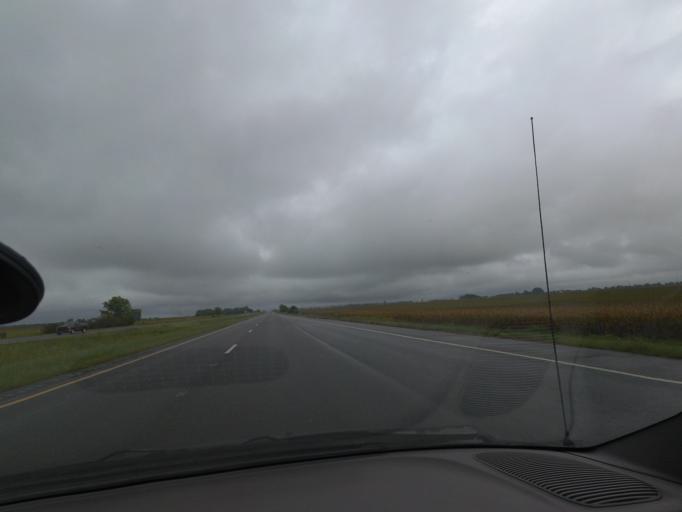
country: US
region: Illinois
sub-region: Champaign County
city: Mahomet
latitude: 40.1203
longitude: -88.4030
